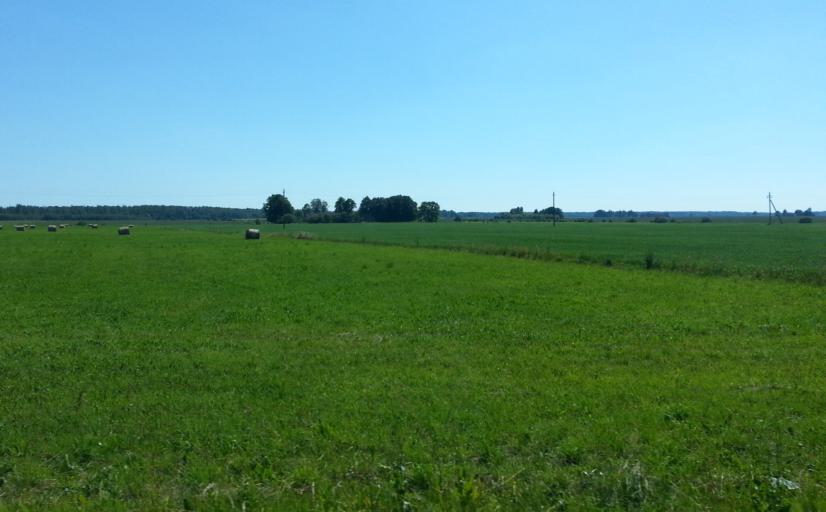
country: LT
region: Panevezys
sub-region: Birzai
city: Birzai
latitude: 56.2298
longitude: 24.5983
